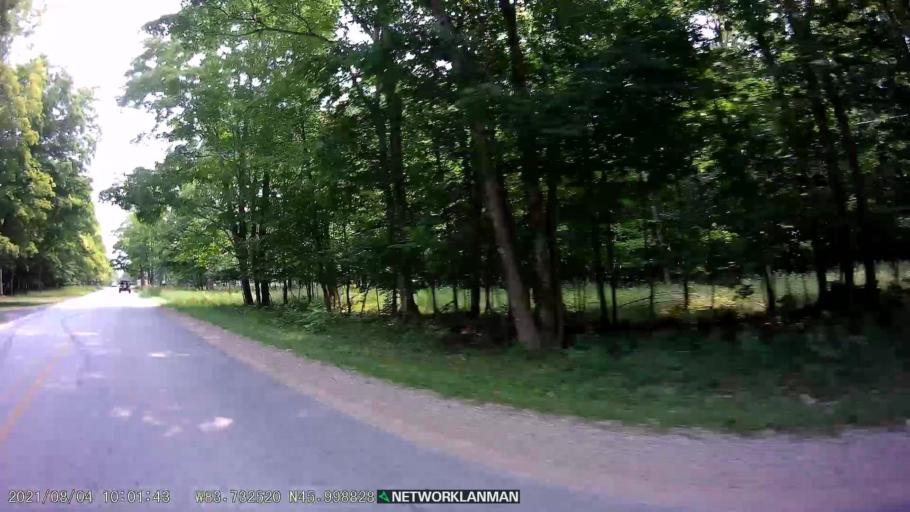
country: CA
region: Ontario
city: Thessalon
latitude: 45.9988
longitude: -83.7320
